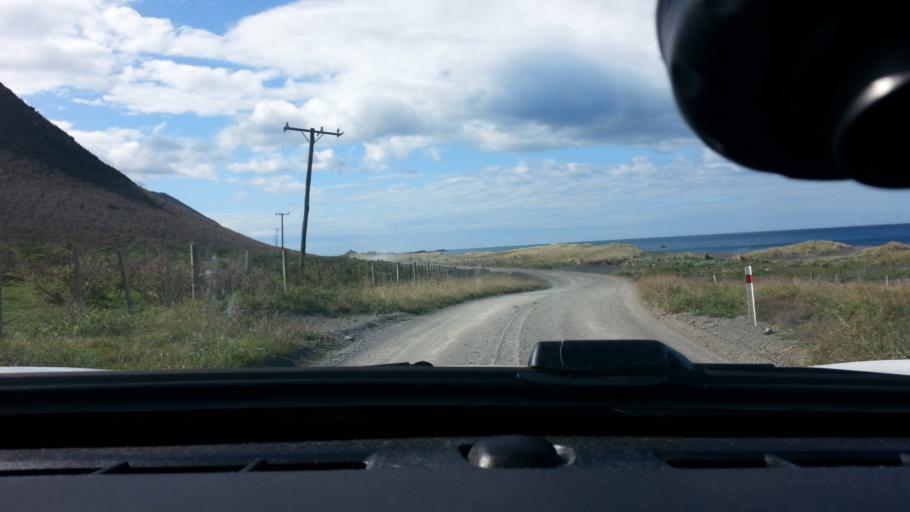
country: NZ
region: Wellington
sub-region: South Wairarapa District
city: Waipawa
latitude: -41.6016
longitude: 175.2460
